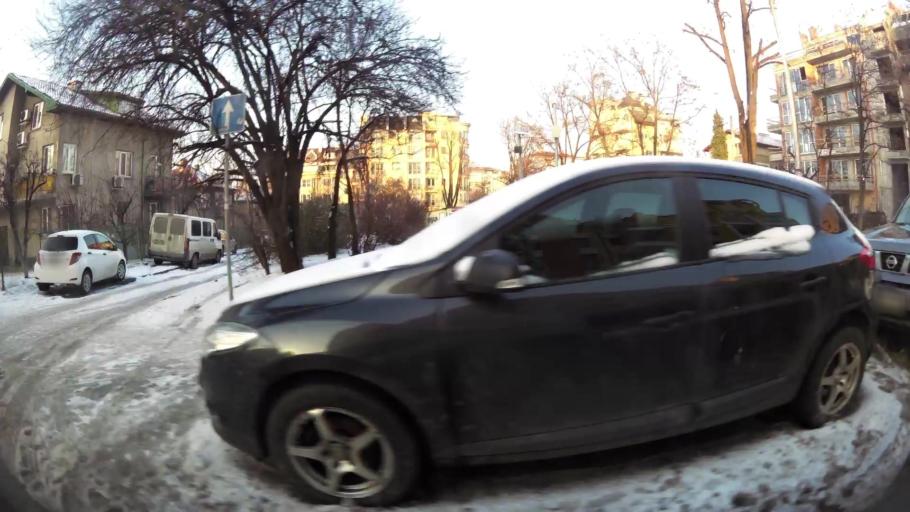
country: BG
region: Sofia-Capital
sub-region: Stolichna Obshtina
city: Sofia
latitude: 42.6912
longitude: 23.3586
